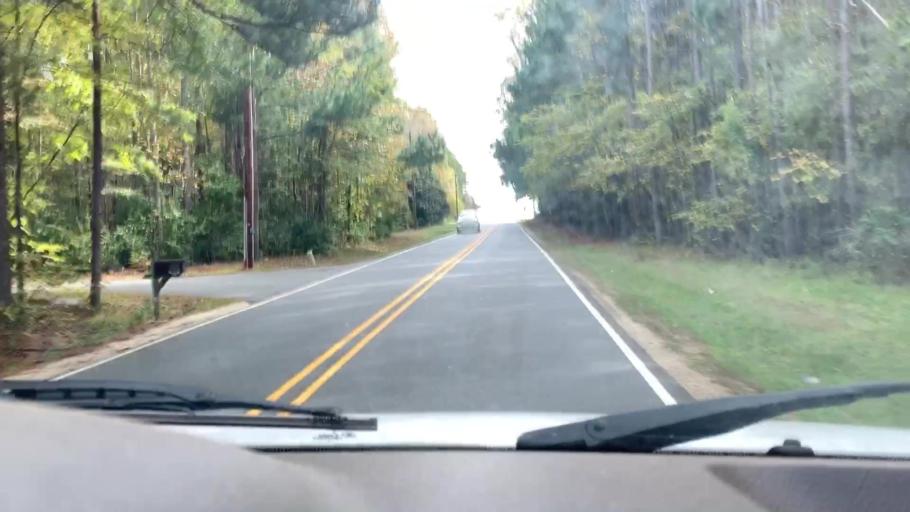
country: US
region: North Carolina
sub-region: Mecklenburg County
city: Huntersville
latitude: 35.4247
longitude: -80.7907
